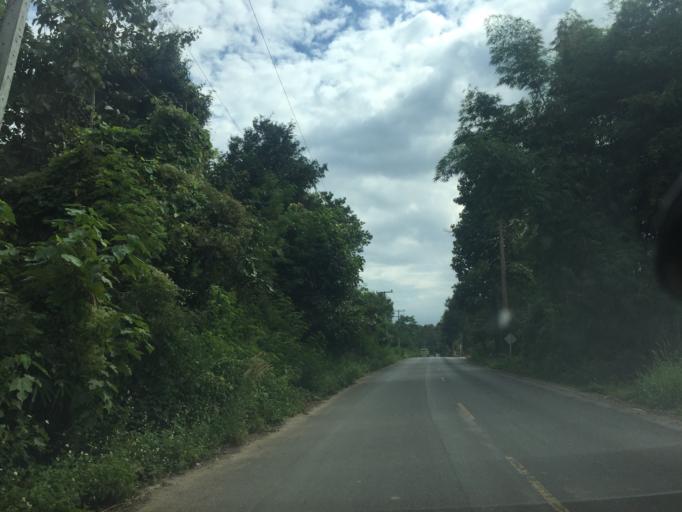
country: TH
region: Lampang
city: Mueang Pan
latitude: 18.8319
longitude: 99.4918
